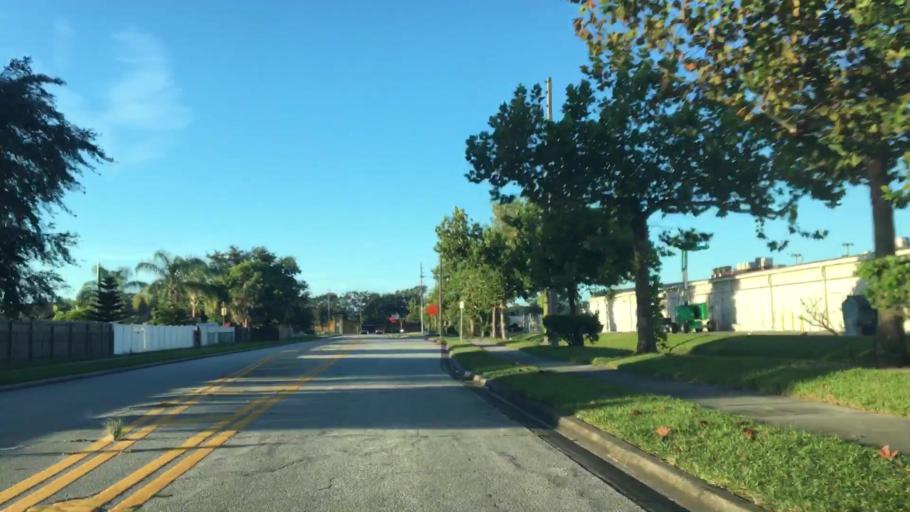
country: US
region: Florida
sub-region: Orange County
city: Conway
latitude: 28.4829
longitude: -81.3068
